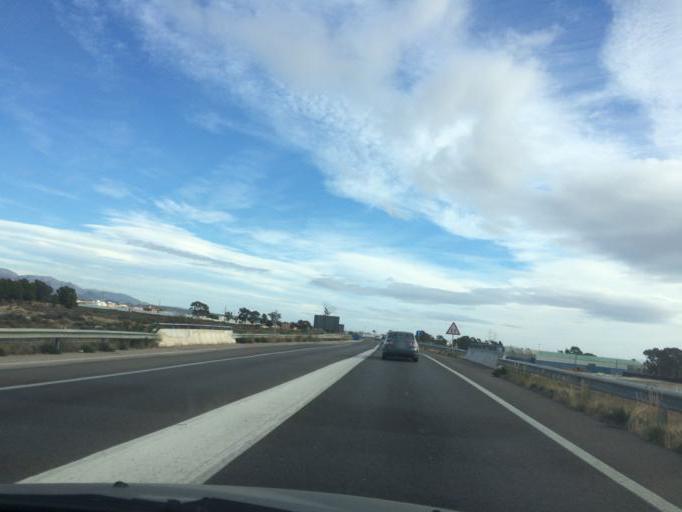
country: ES
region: Andalusia
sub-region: Provincia de Almeria
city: Viator
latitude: 36.8495
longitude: -2.3808
